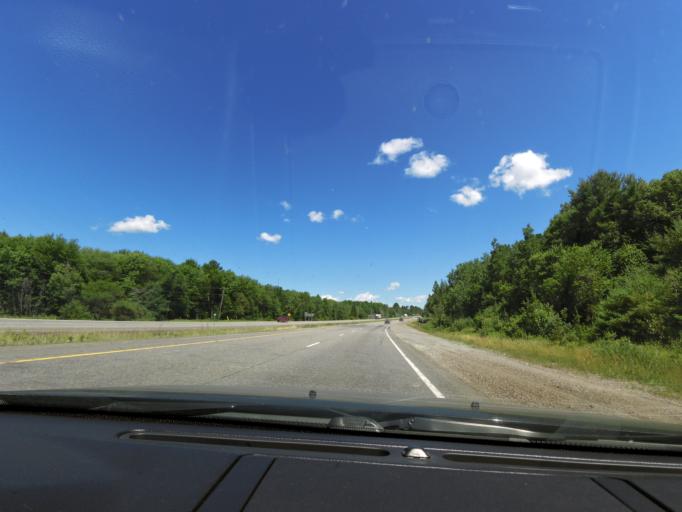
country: CA
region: Ontario
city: Bracebridge
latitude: 45.0630
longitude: -79.2968
